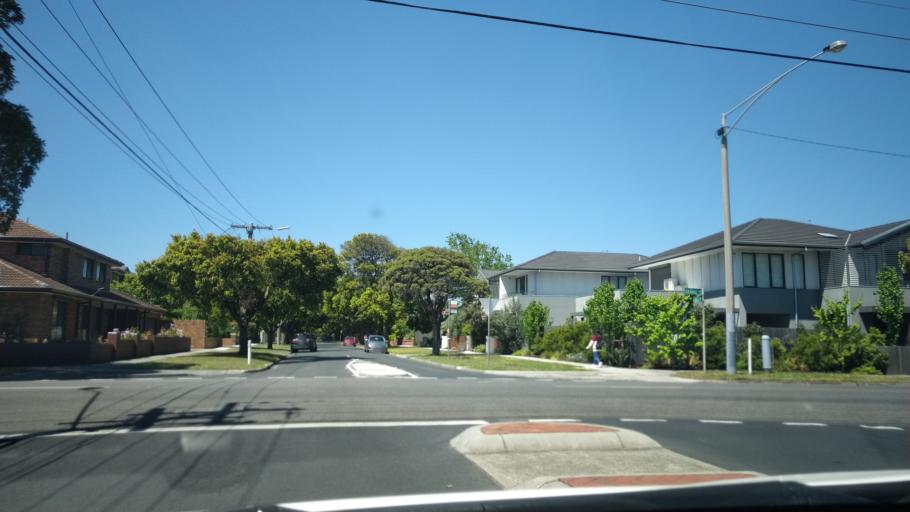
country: AU
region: Victoria
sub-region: Glen Eira
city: Glen Huntly
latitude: -37.9004
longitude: 145.0445
